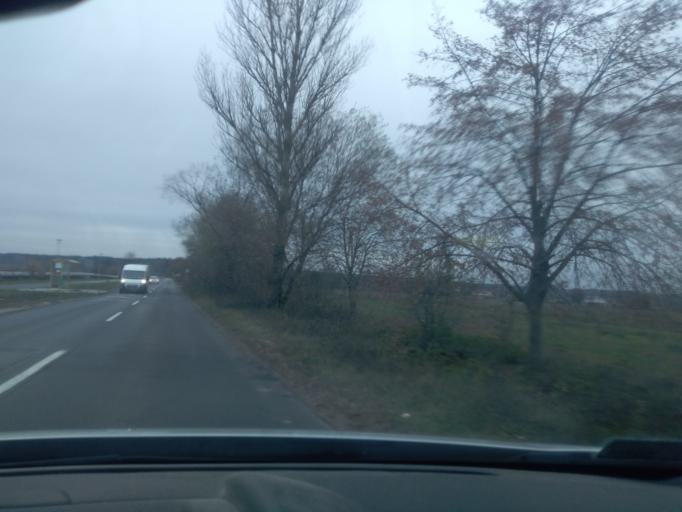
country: PL
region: Greater Poland Voivodeship
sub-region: Powiat poznanski
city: Murowana Goslina
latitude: 52.5605
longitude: 16.9813
